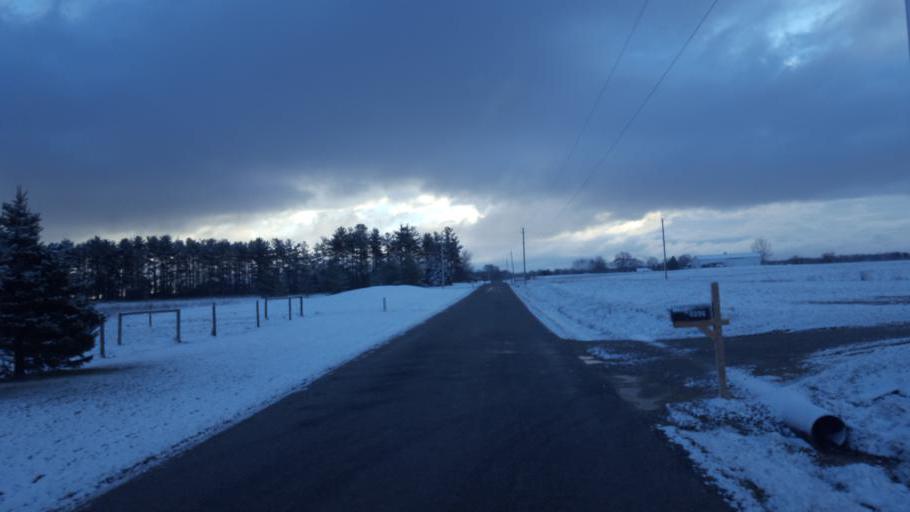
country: US
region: Ohio
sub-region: Morrow County
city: Mount Gilead
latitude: 40.5890
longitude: -82.8311
